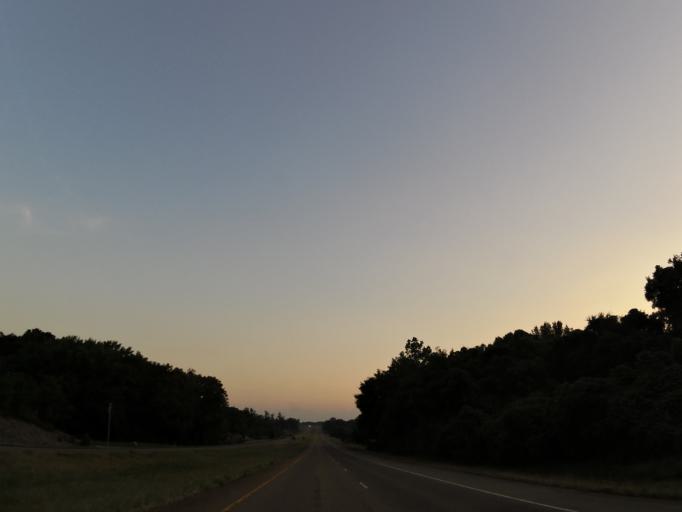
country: US
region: Tennessee
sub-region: Carroll County
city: McKenzie
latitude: 36.1607
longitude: -88.4609
